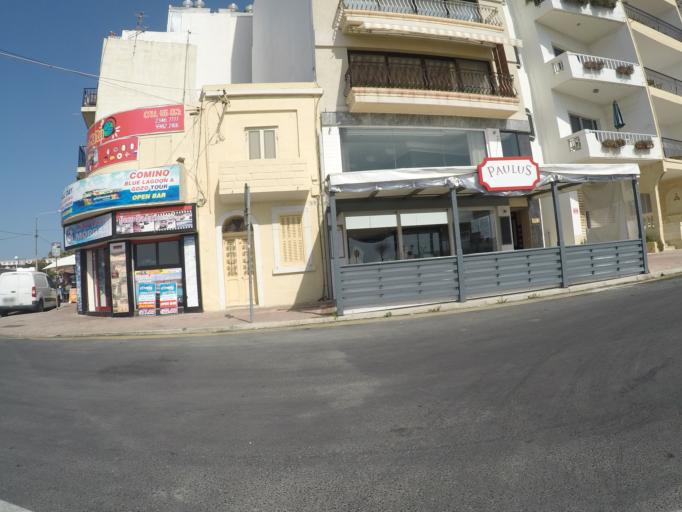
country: MT
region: Saint Paul's Bay
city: San Pawl il-Bahar
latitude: 35.9520
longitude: 14.4089
